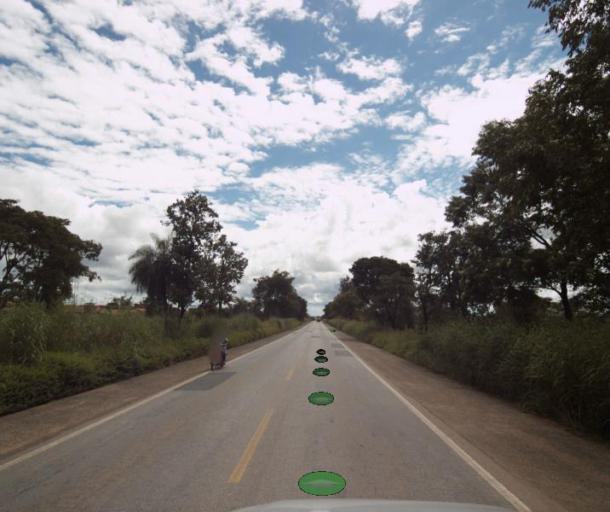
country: BR
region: Goias
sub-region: Uruacu
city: Uruacu
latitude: -14.3294
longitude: -49.1534
